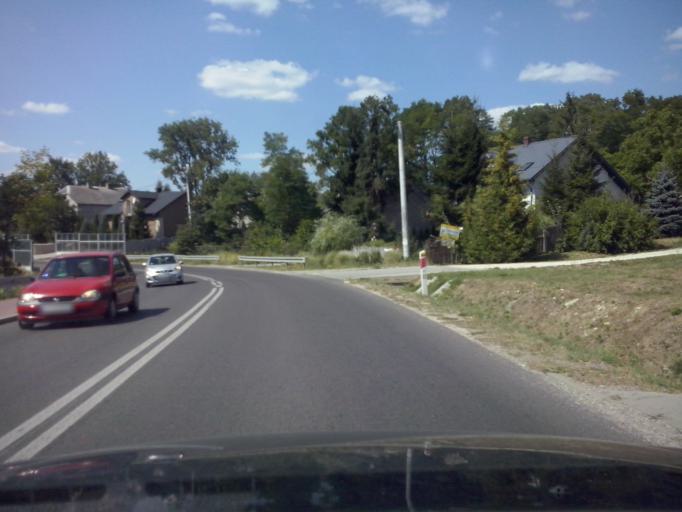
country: PL
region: Swietokrzyskie
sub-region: Powiat buski
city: Gnojno
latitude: 50.6021
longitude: 20.8499
